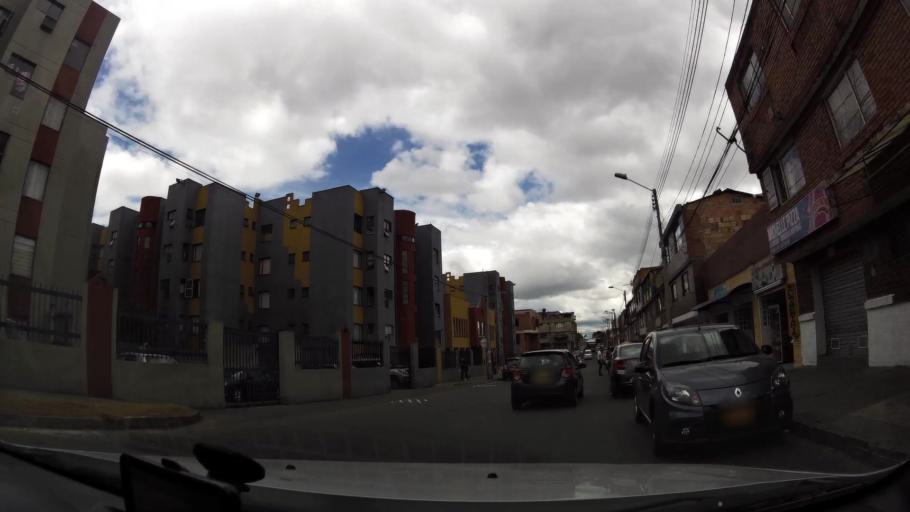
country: CO
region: Bogota D.C.
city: Bogota
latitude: 4.6207
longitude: -74.1236
